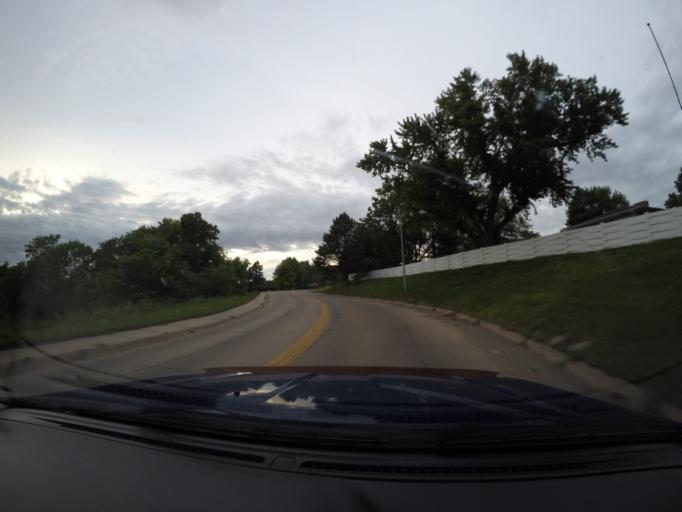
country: US
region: Nebraska
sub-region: Buffalo County
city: Kearney
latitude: 40.7057
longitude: -99.0984
